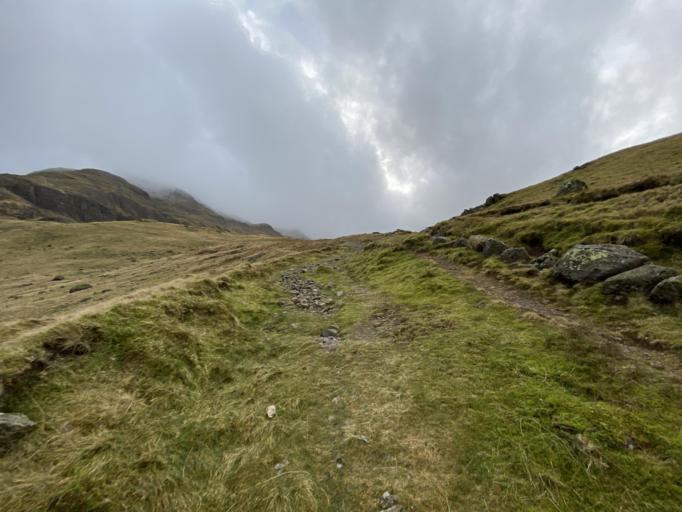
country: GB
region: England
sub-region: Cumbria
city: Keswick
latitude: 54.4771
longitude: -3.2048
